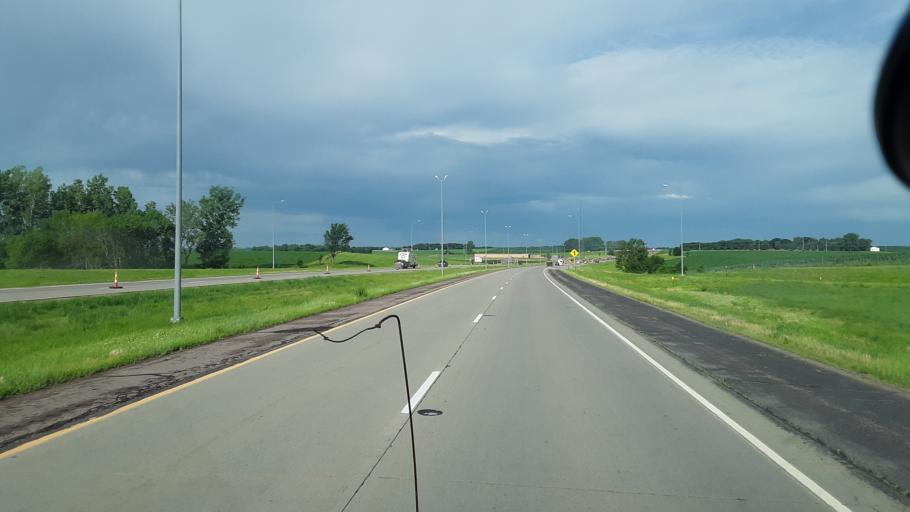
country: US
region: South Dakota
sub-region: Minnehaha County
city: Crooks
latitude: 43.6113
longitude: -96.7900
